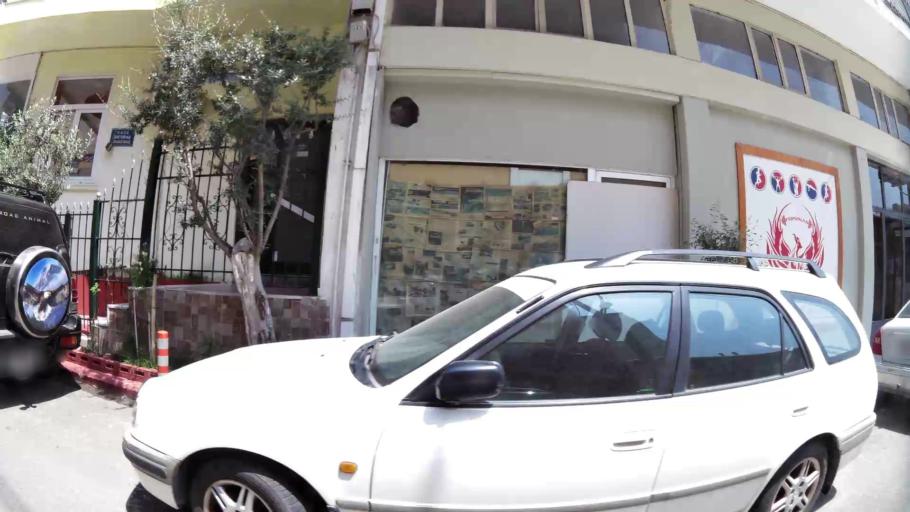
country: GR
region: Central Macedonia
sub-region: Nomos Thessalonikis
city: Evosmos
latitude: 40.6655
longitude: 22.9076
